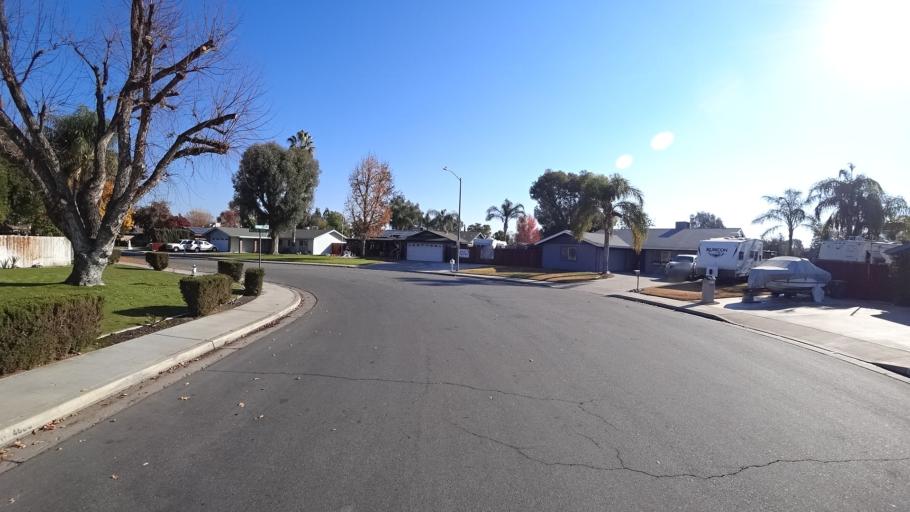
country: US
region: California
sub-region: Kern County
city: Greenfield
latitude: 35.3078
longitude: -119.0552
